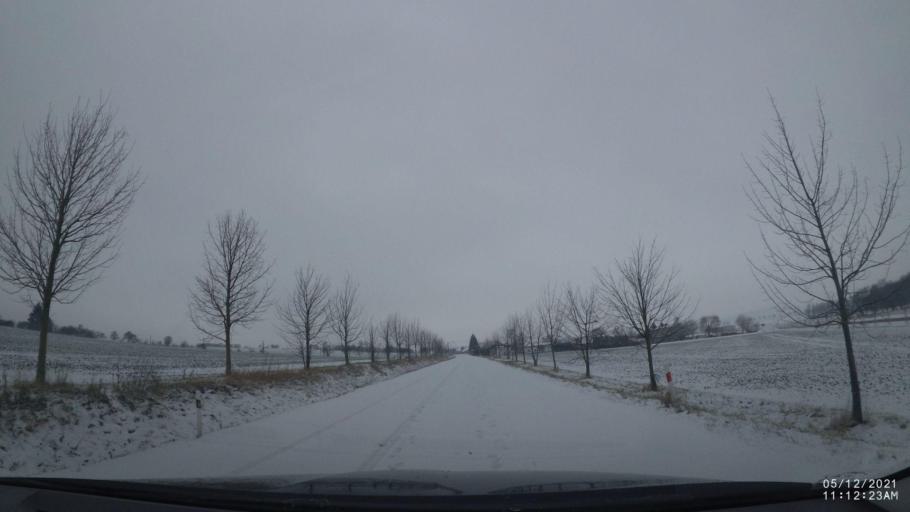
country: CZ
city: Solnice
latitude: 50.1857
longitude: 16.2248
